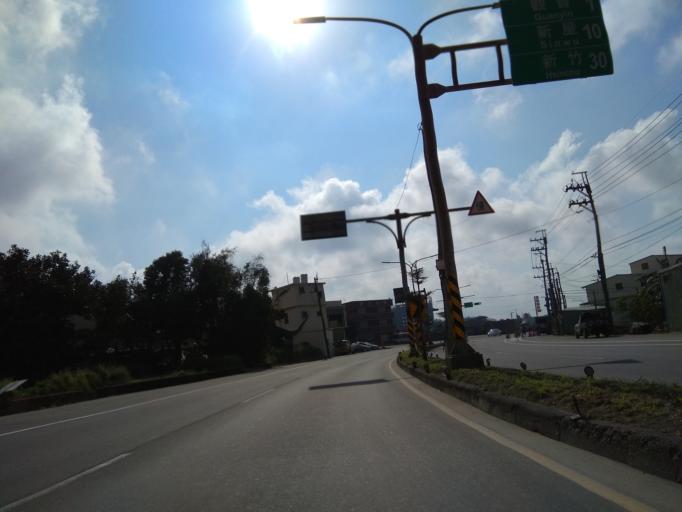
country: TW
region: Taiwan
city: Taoyuan City
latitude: 25.0356
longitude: 121.1029
